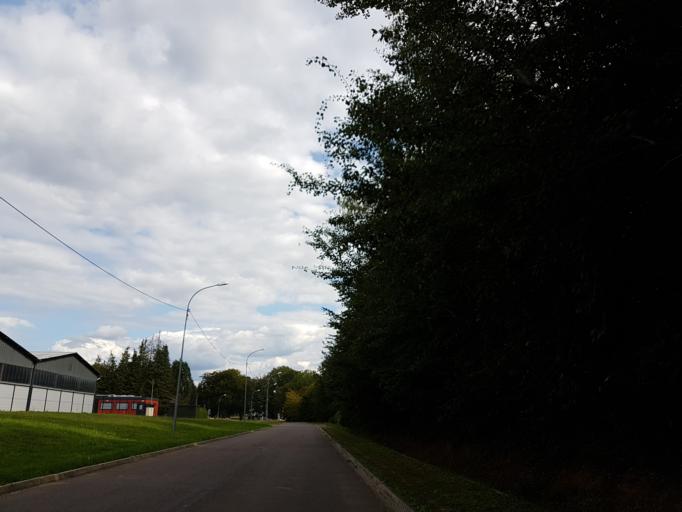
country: FR
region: Franche-Comte
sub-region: Departement de la Haute-Saone
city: Luxeuil-les-Bains
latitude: 47.8147
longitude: 6.3573
